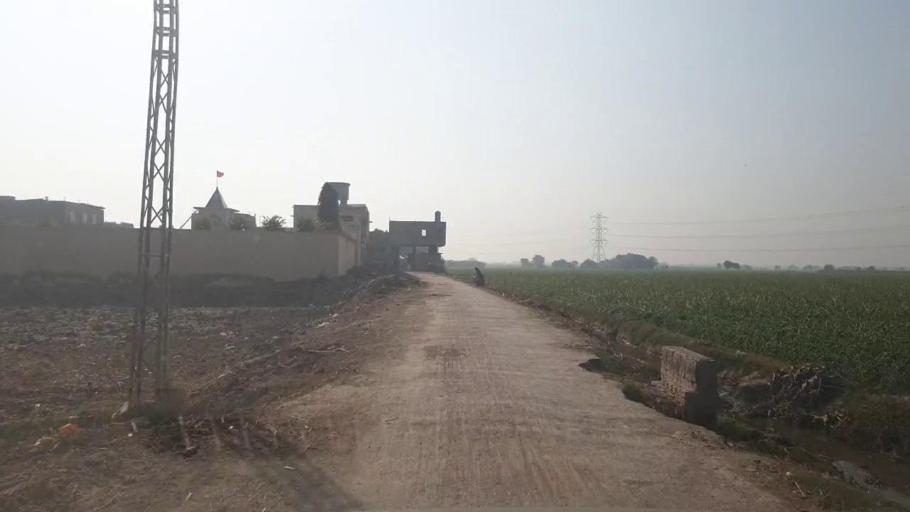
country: PK
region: Sindh
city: Tando Allahyar
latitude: 25.4729
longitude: 68.7512
